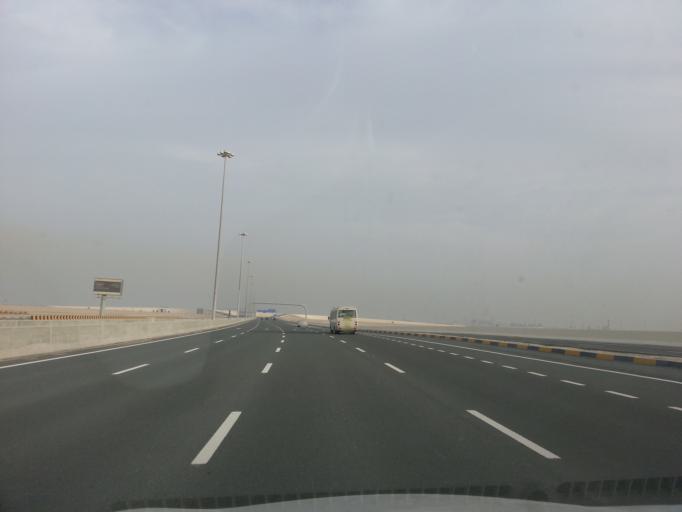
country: AE
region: Abu Dhabi
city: Abu Dhabi
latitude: 24.7605
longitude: 54.7311
